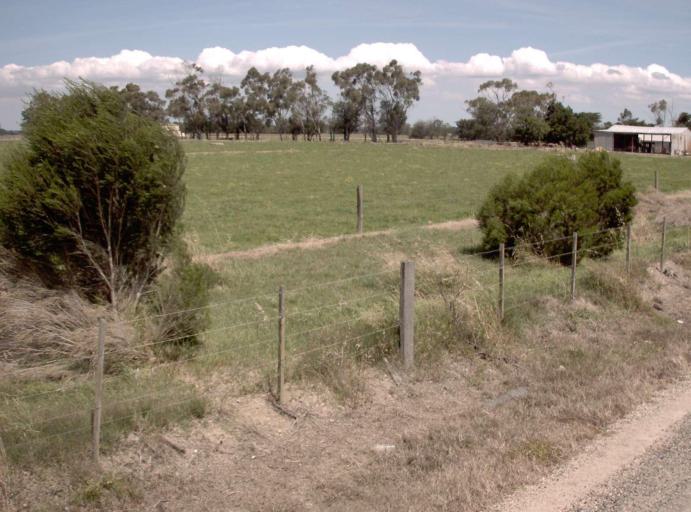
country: AU
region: Victoria
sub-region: Wellington
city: Heyfield
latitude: -38.0406
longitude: 146.8771
